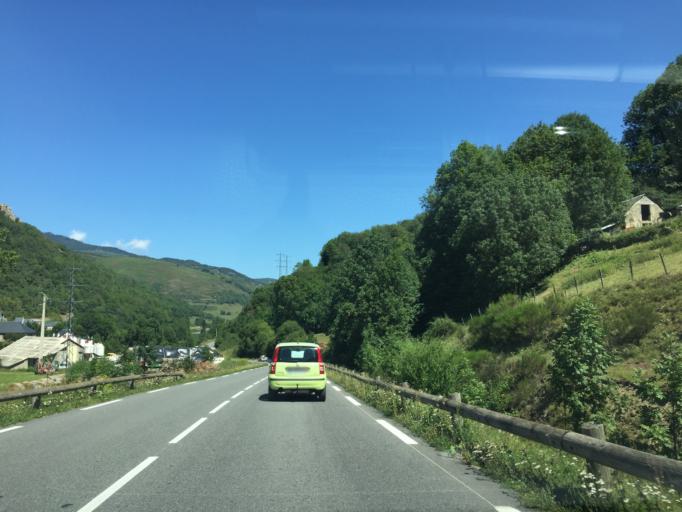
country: FR
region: Midi-Pyrenees
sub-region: Departement des Hautes-Pyrenees
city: Saint-Lary-Soulan
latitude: 42.8883
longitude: 0.3527
